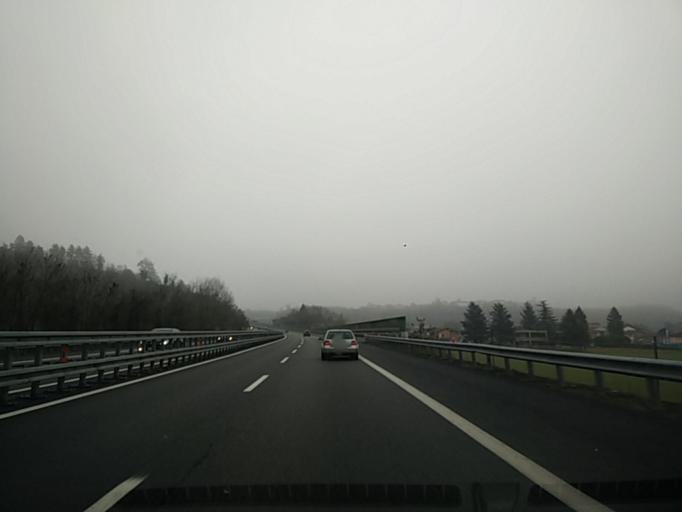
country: IT
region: Piedmont
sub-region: Provincia di Asti
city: Azzano d'Asti
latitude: 44.9086
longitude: 8.2773
